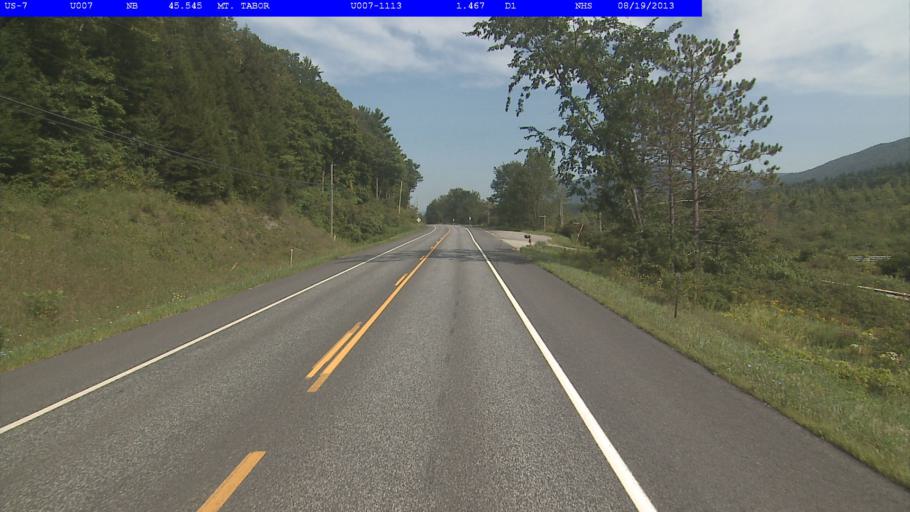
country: US
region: Vermont
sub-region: Bennington County
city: Manchester Center
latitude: 43.3260
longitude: -72.9913
